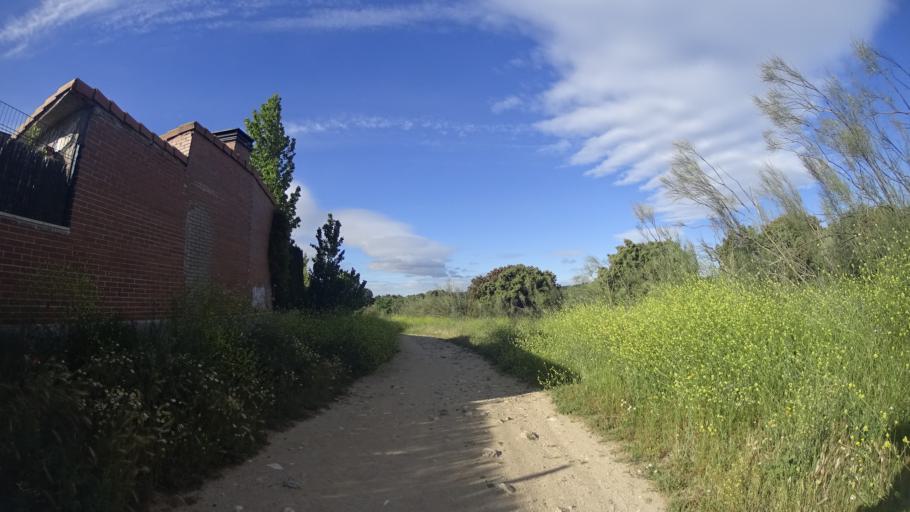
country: ES
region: Madrid
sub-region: Provincia de Madrid
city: Torrelodones
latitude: 40.5269
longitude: -3.9356
